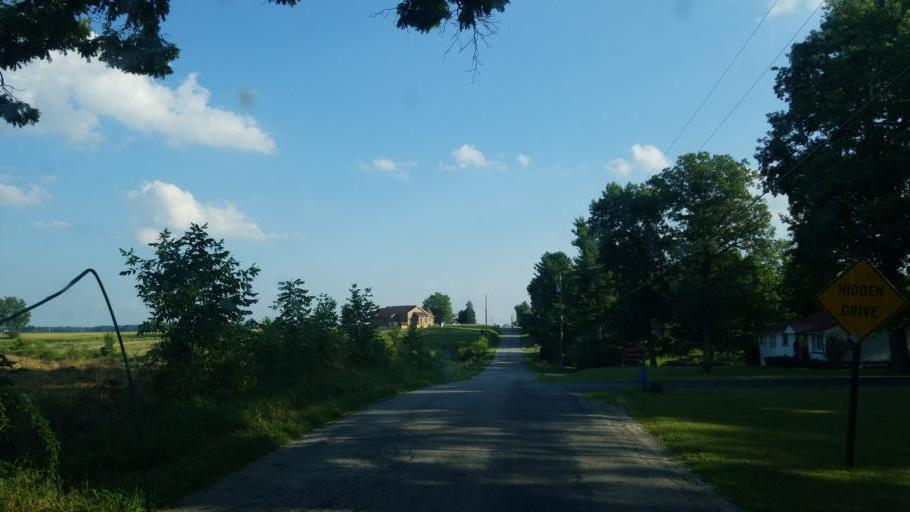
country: US
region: Ohio
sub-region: Crawford County
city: Bucyrus
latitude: 40.8173
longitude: -82.9020
